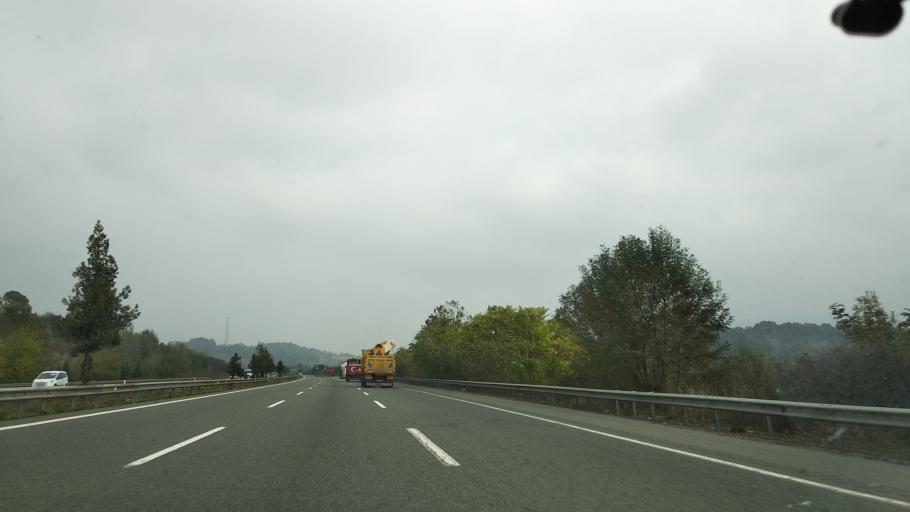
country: TR
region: Sakarya
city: Hendek
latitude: 40.7602
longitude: 30.7521
